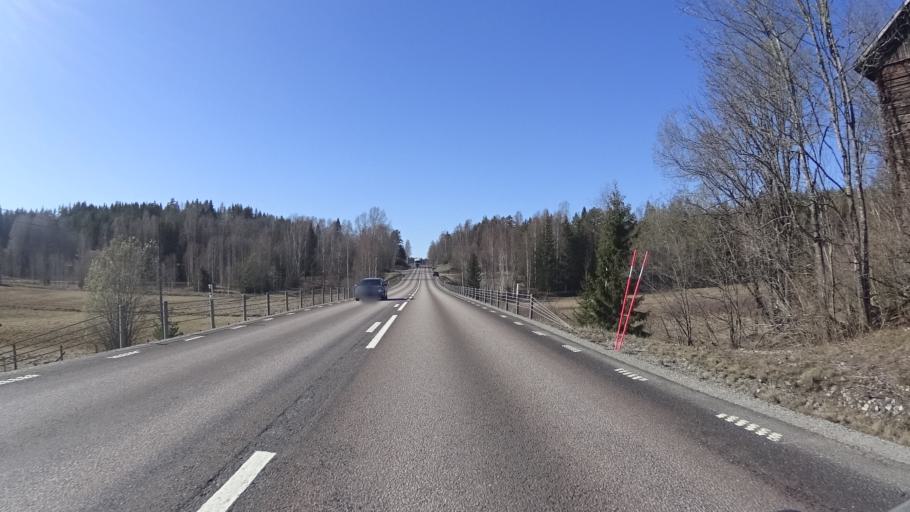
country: SE
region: Vaermland
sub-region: Sunne Kommun
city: Sunne
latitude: 59.6628
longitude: 12.9229
